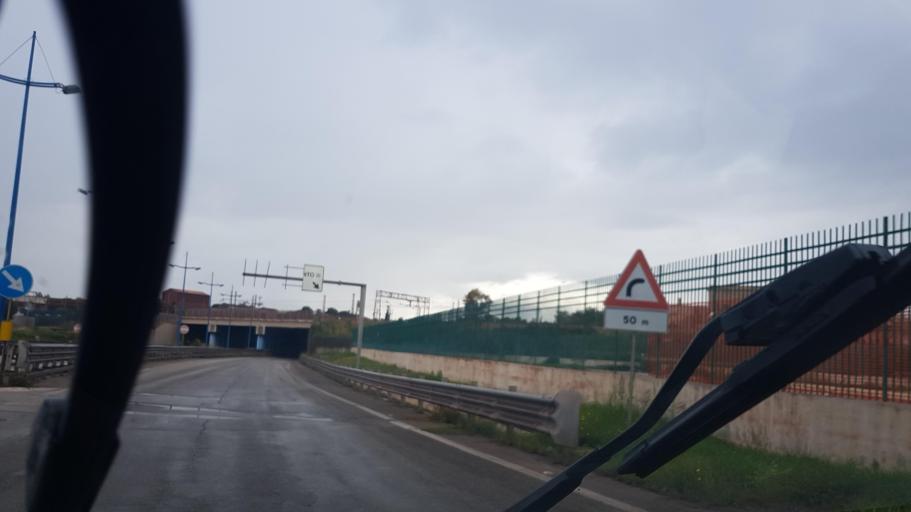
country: IT
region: Apulia
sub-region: Provincia di Taranto
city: Statte
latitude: 40.4810
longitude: 17.2078
